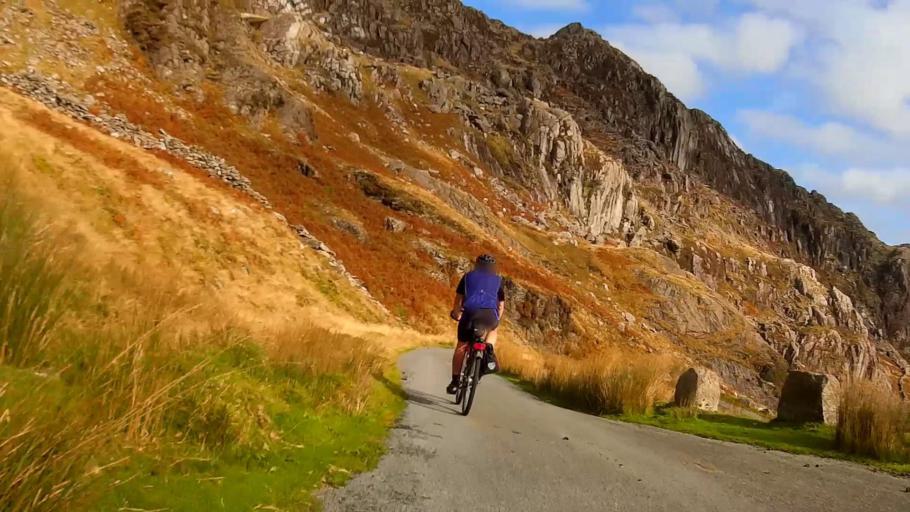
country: GB
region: Wales
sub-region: Gwynedd
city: Maentwrog
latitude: 52.9813
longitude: -3.9822
